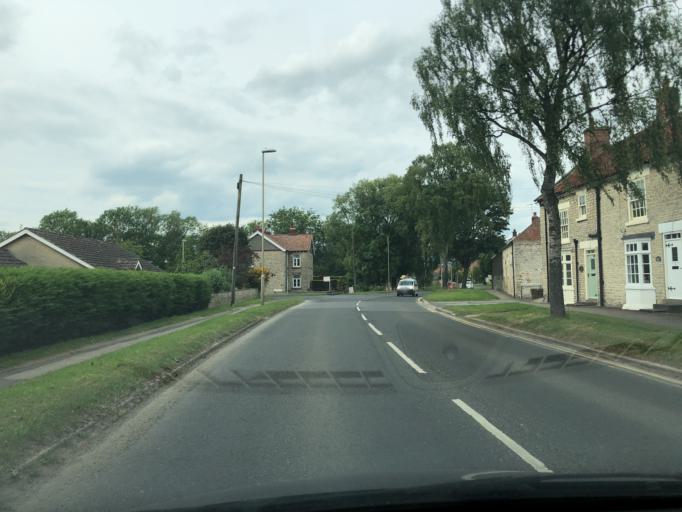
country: GB
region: England
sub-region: North Yorkshire
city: Pickering
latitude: 54.2491
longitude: -0.7917
